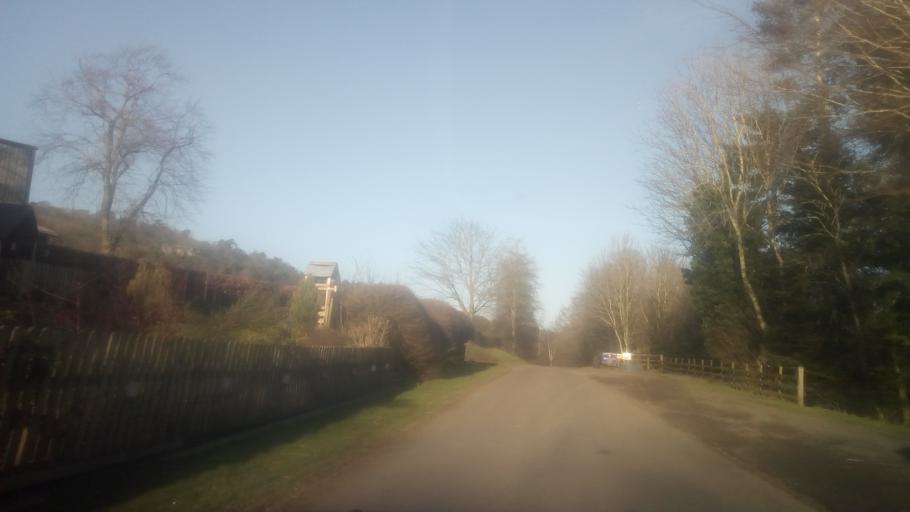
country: GB
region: Scotland
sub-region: The Scottish Borders
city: Saint Boswells
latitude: 55.4720
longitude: -2.6670
